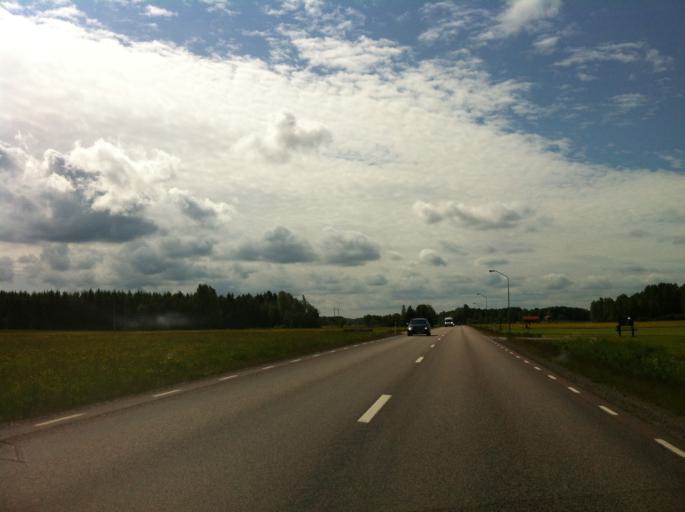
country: SE
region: Vaermland
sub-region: Karlstads Kommun
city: Edsvalla
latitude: 59.4876
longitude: 13.2180
